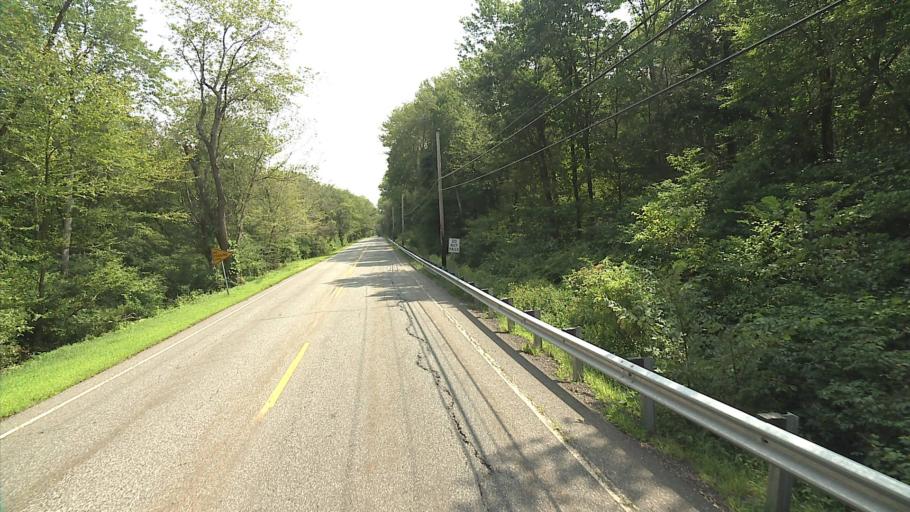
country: US
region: Connecticut
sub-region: New London County
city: Montville Center
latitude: 41.5026
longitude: -72.1890
